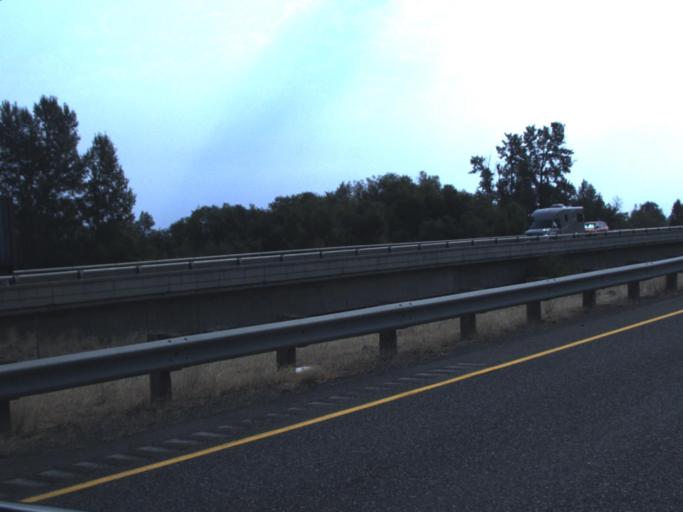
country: US
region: Washington
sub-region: Kittitas County
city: Ellensburg
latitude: 47.0205
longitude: -120.6102
